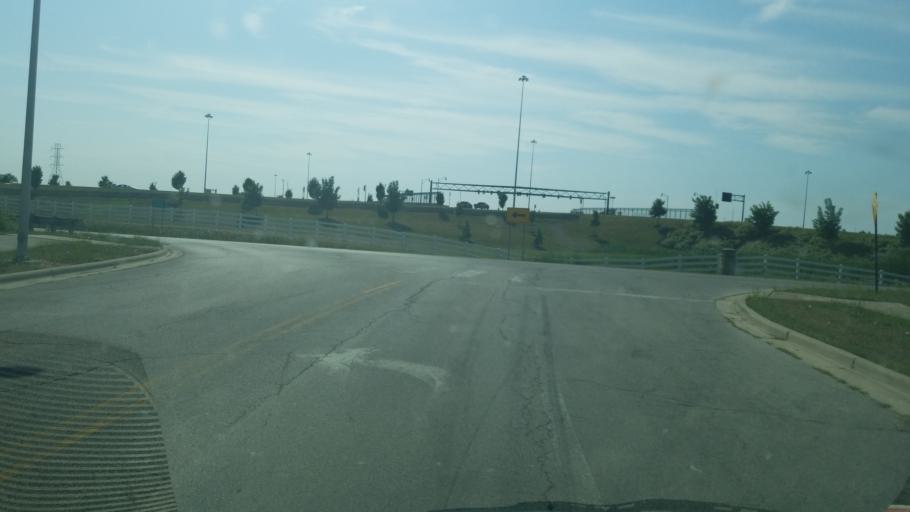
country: US
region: Ohio
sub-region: Franklin County
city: Grove City
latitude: 39.8415
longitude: -83.0926
